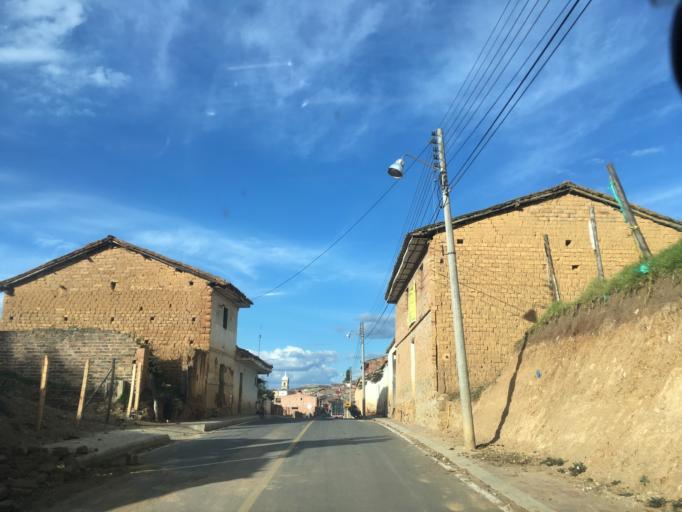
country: CO
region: Boyaca
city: Pesca
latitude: 5.5529
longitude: -73.0536
